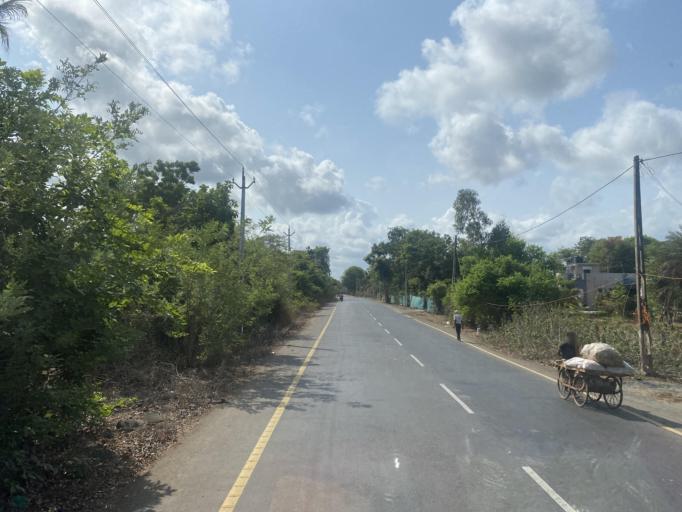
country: IN
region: Daman and Diu
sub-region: Daman District
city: Daman
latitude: 20.3356
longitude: 72.8036
